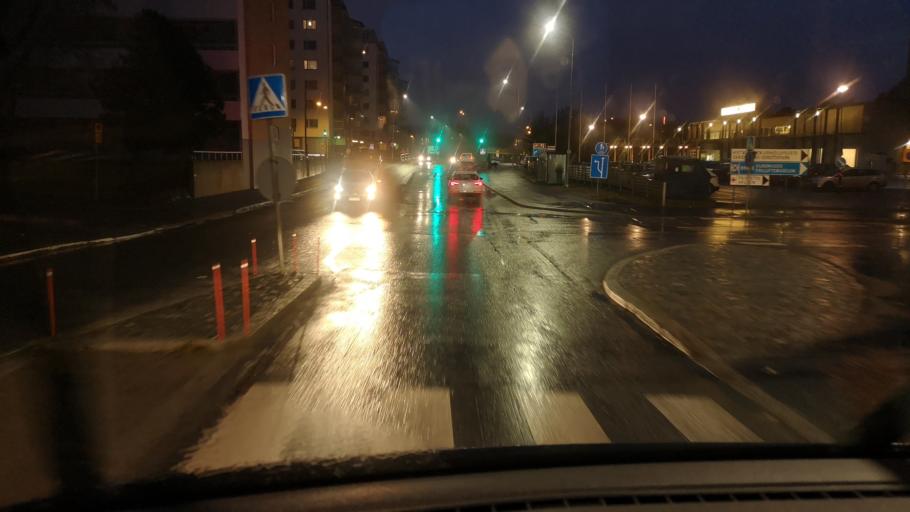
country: FI
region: Ostrobothnia
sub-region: Vaasa
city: Vaasa
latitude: 63.0869
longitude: 21.6182
